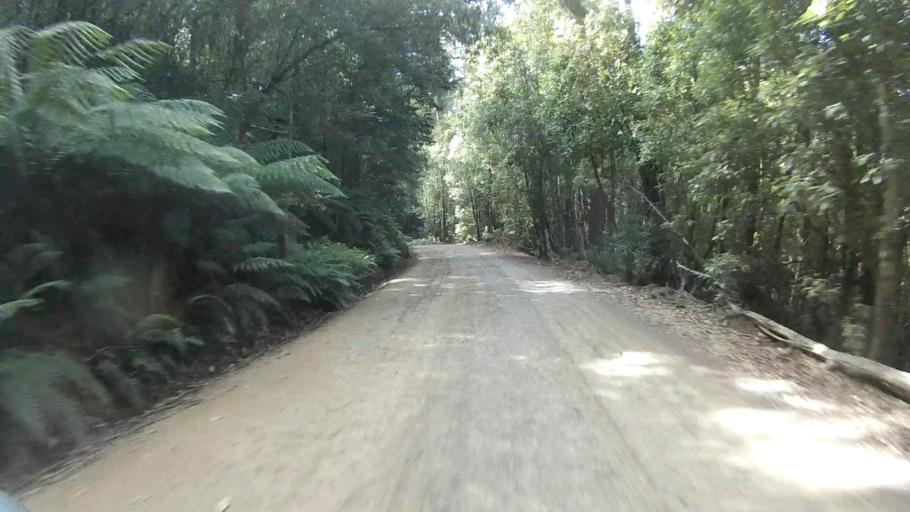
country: AU
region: Tasmania
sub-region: Derwent Valley
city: New Norfolk
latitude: -42.6762
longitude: 146.6945
